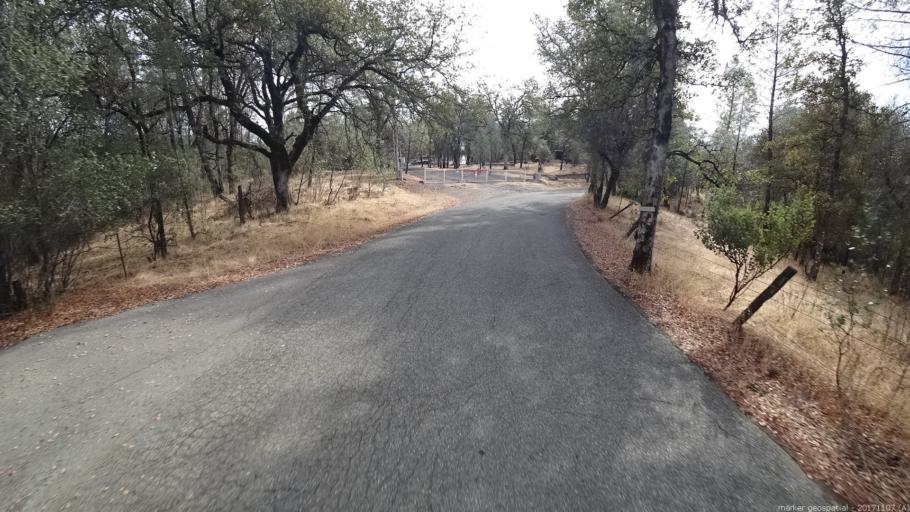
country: US
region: California
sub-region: Shasta County
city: Shasta
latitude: 40.5223
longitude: -122.5526
